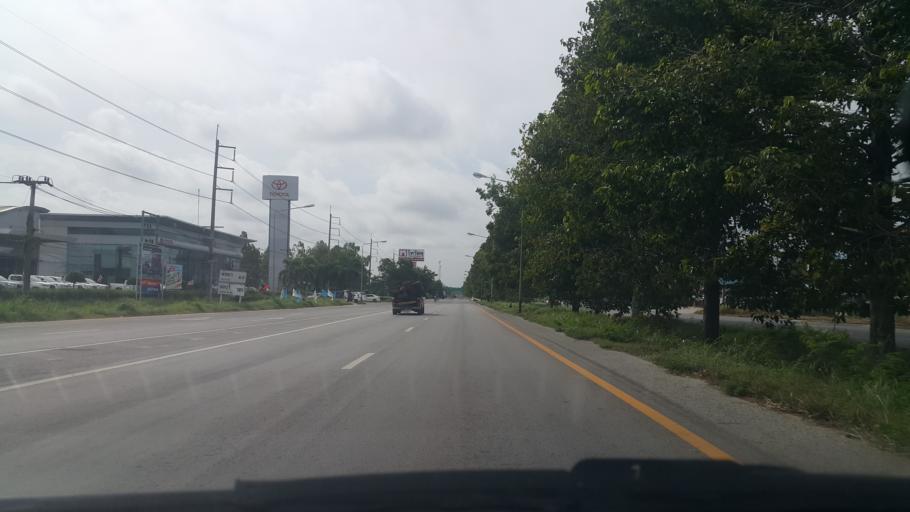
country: TH
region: Rayong
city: Rayong
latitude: 12.6659
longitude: 101.3081
